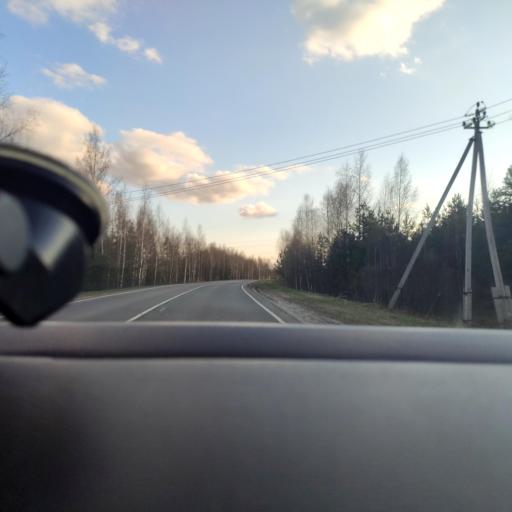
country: RU
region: Moskovskaya
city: Shaturtorf
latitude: 55.4383
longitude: 39.4310
